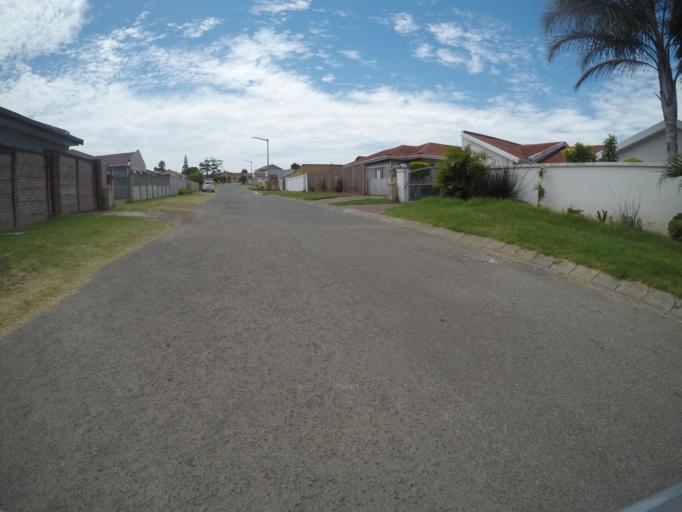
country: ZA
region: Eastern Cape
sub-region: Buffalo City Metropolitan Municipality
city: East London
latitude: -32.9803
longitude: 27.8612
